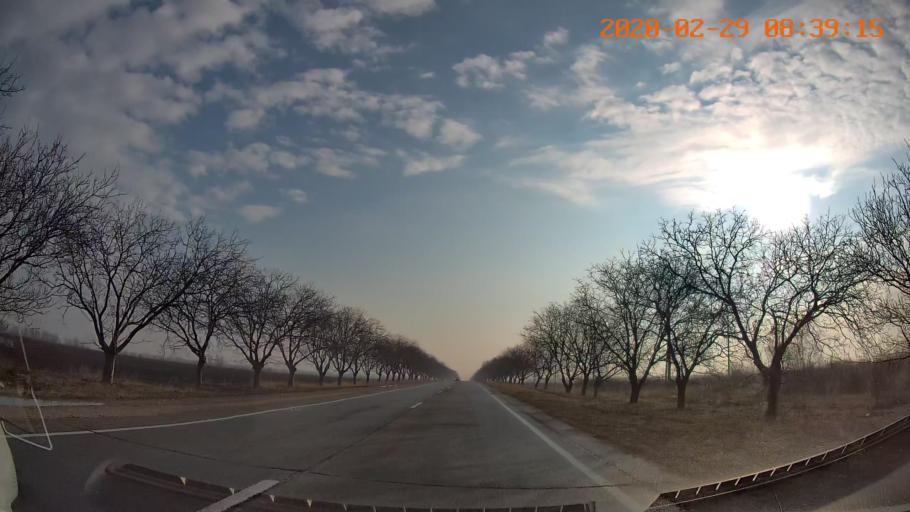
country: MD
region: Anenii Noi
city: Varnita
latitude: 46.9223
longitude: 29.3940
